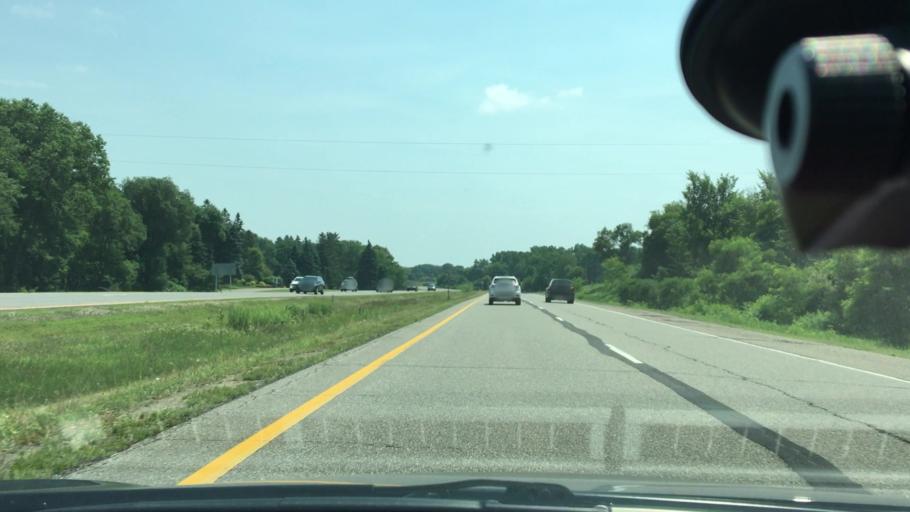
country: US
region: Minnesota
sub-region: Hennepin County
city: Plymouth
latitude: 44.9937
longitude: -93.4356
